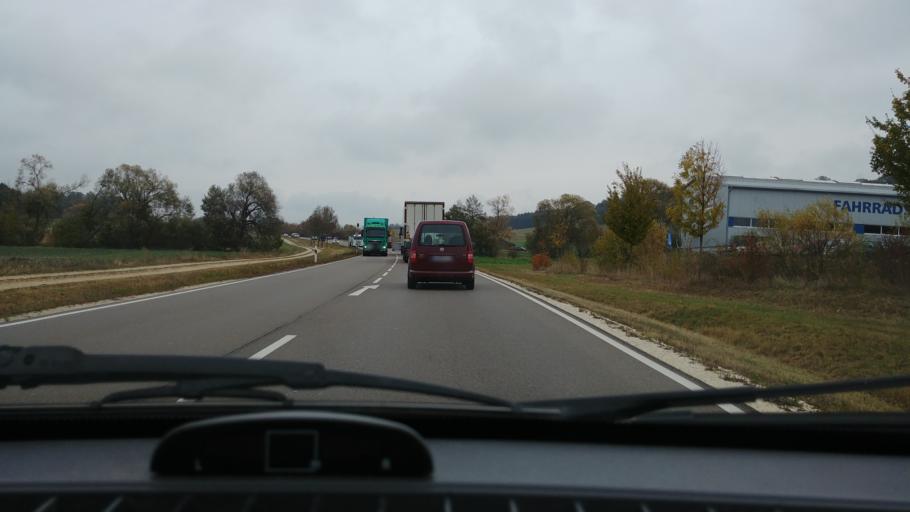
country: DE
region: Baden-Wuerttemberg
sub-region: Regierungsbezirk Stuttgart
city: Huttlingen
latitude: 48.8854
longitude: 10.1347
